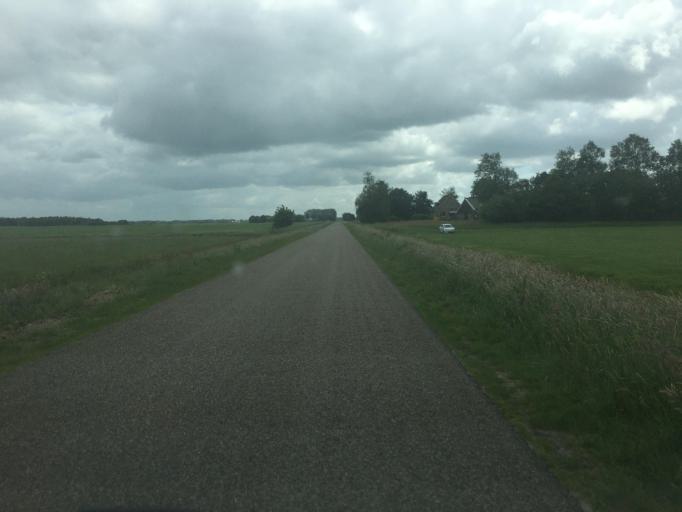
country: NL
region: Friesland
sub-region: Gemeente Heerenveen
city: Nieuwehorne
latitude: 52.9333
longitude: 6.0240
